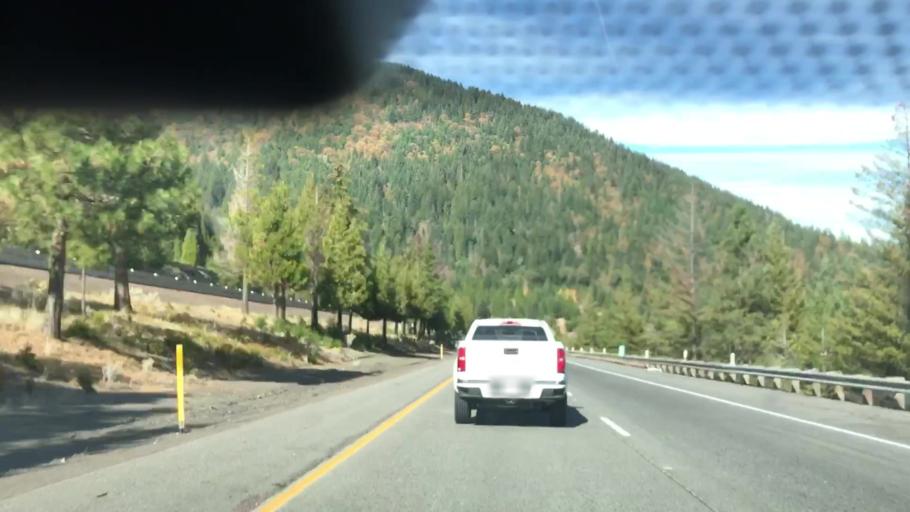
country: US
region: Oregon
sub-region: Jackson County
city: Ashland
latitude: 42.0687
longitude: -122.6022
